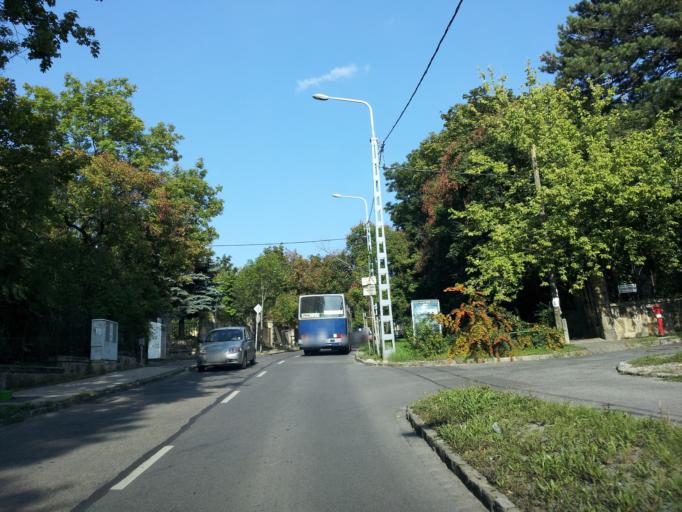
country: HU
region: Budapest
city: Budapest II. keruelet
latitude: 47.5173
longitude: 19.0053
